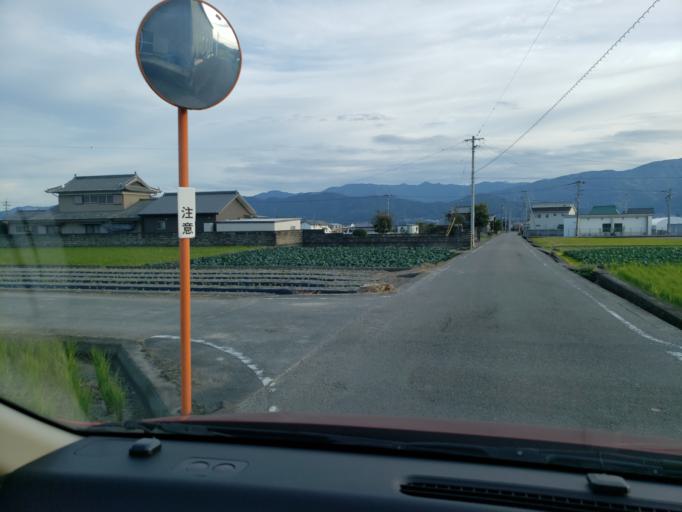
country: JP
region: Tokushima
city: Wakimachi
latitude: 34.0914
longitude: 134.2257
